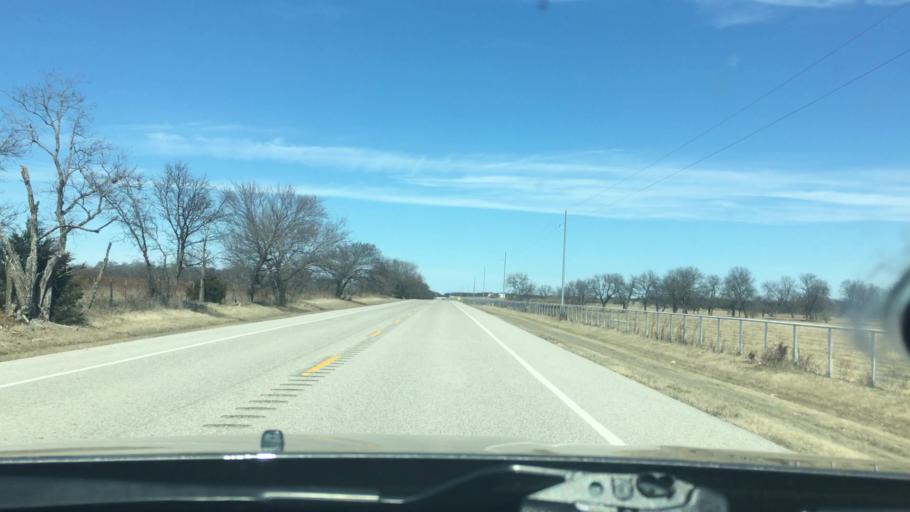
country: US
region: Oklahoma
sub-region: Murray County
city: Sulphur
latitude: 34.3669
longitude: -96.9508
